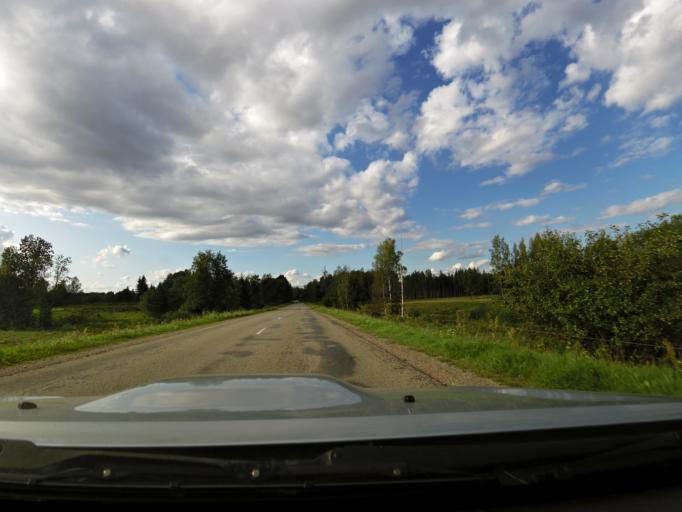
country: LV
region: Akniste
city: Akniste
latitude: 56.0674
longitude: 25.8927
